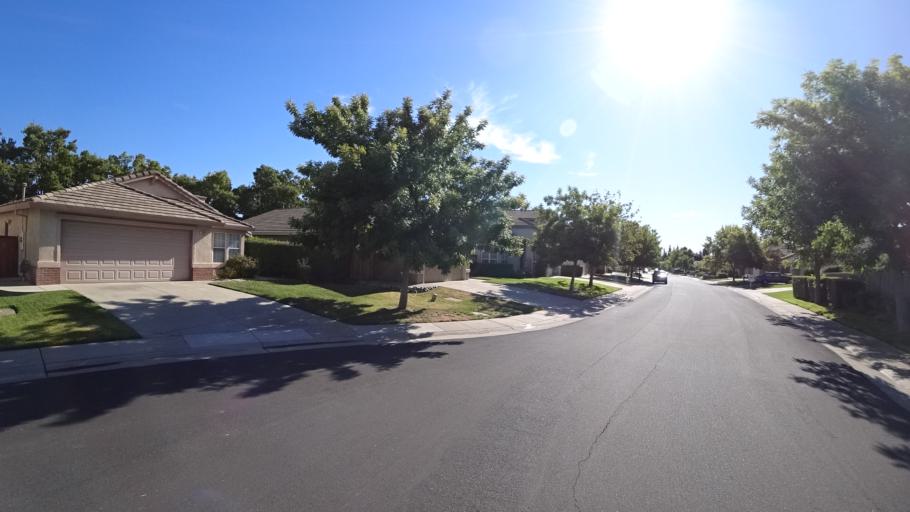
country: US
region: California
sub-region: Sacramento County
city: Laguna
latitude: 38.4083
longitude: -121.4735
